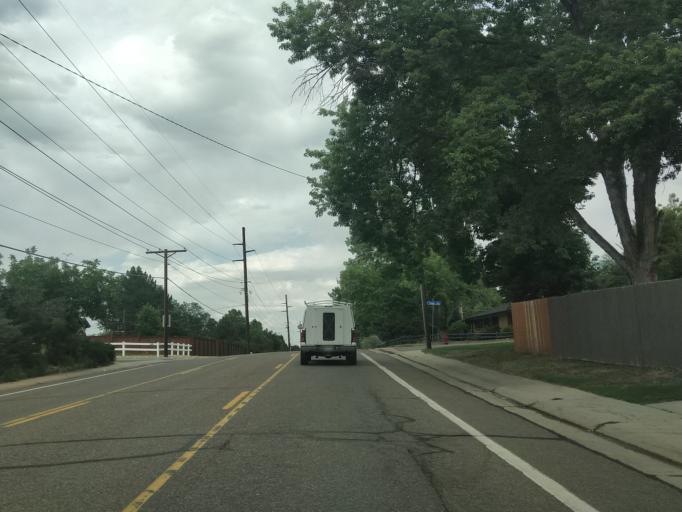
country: US
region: Colorado
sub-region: Jefferson County
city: Lakewood
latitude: 39.6966
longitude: -105.0938
